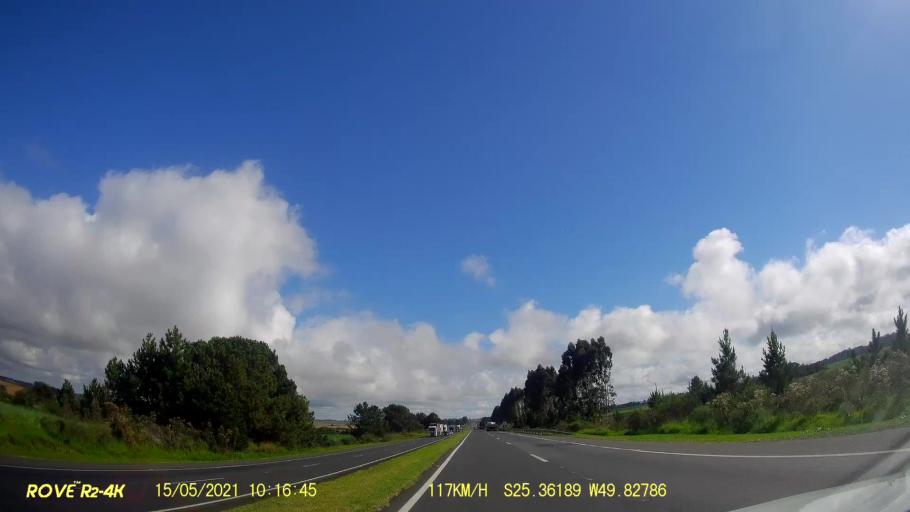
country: BR
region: Parana
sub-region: Palmeira
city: Palmeira
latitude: -25.3613
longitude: -49.8296
